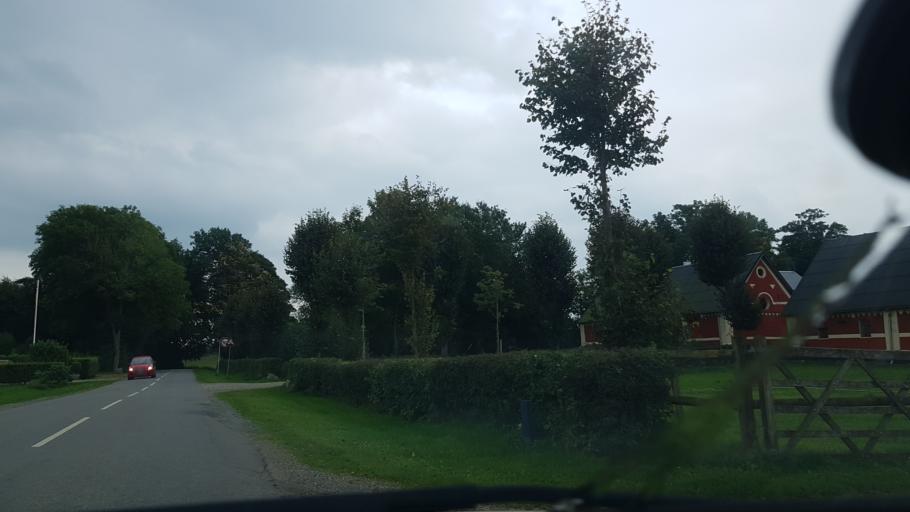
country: DK
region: South Denmark
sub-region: Kolding Kommune
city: Lunderskov
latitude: 55.5275
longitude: 9.3474
